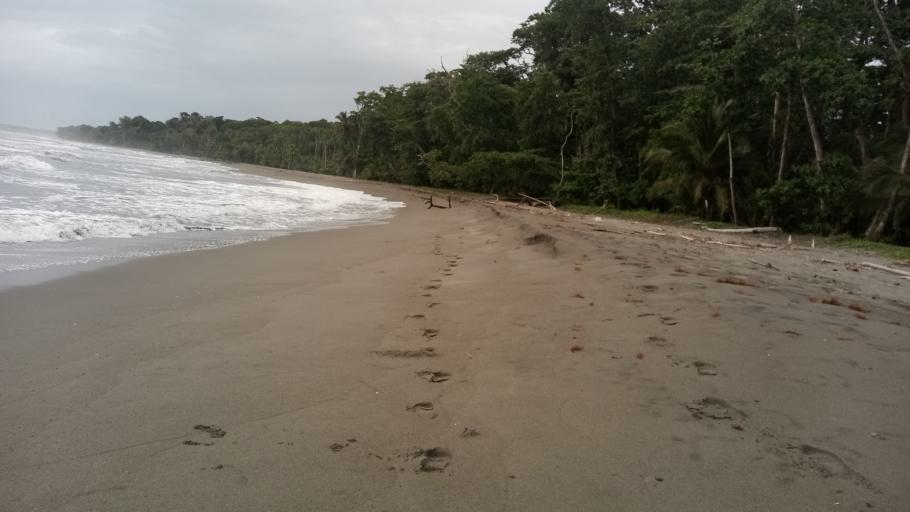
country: CR
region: Limon
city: Sixaola
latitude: 9.6165
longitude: -82.6203
